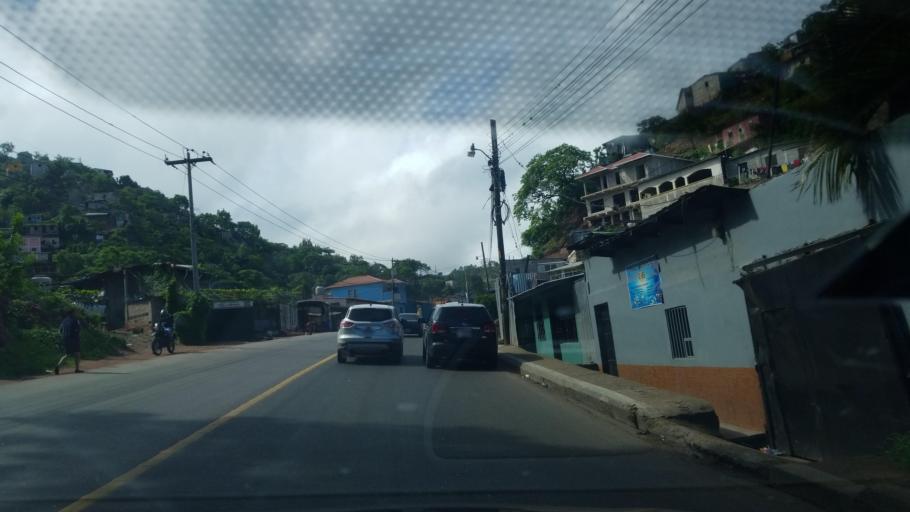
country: HN
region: Francisco Morazan
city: El Tablon
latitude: 14.0567
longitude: -87.1586
